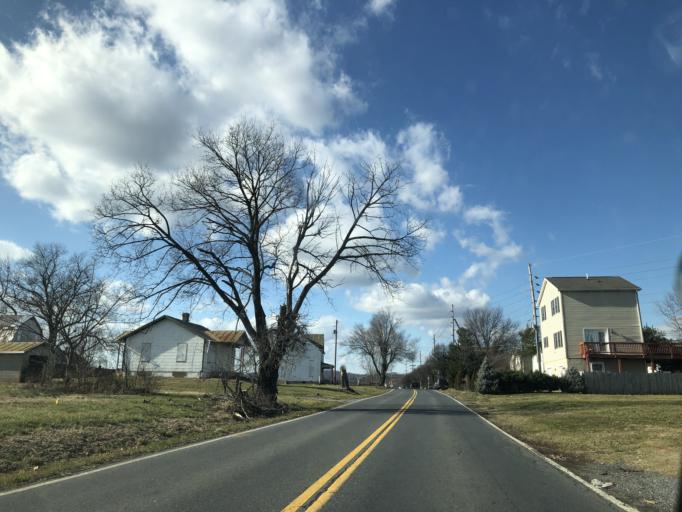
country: US
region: Maryland
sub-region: Frederick County
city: Ballenger Creek
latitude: 39.4083
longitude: -77.4504
